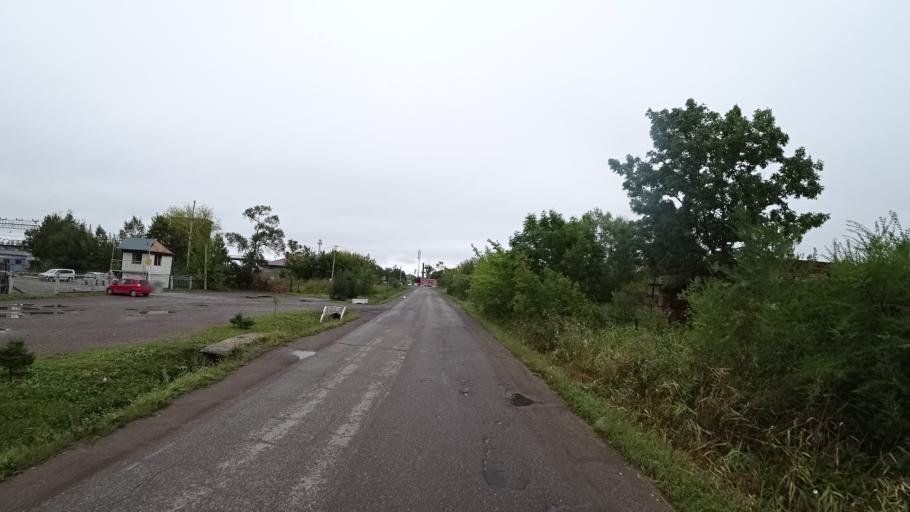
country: RU
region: Primorskiy
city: Monastyrishche
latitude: 44.2039
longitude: 132.4402
